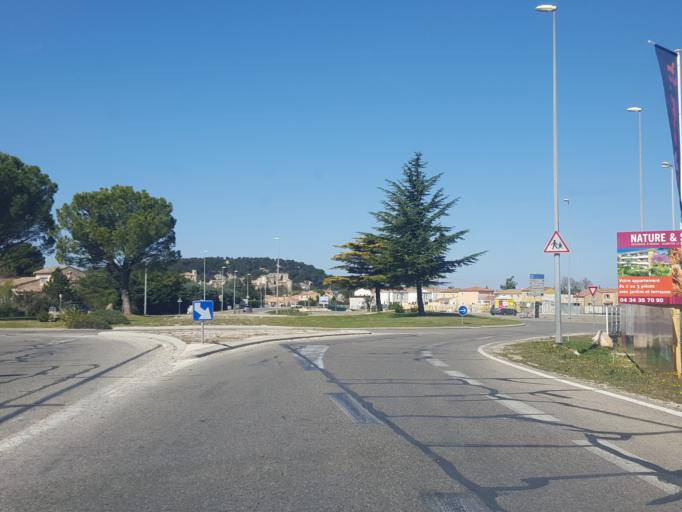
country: FR
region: Provence-Alpes-Cote d'Azur
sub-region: Departement du Vaucluse
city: Vedene
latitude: 43.9729
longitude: 4.9134
